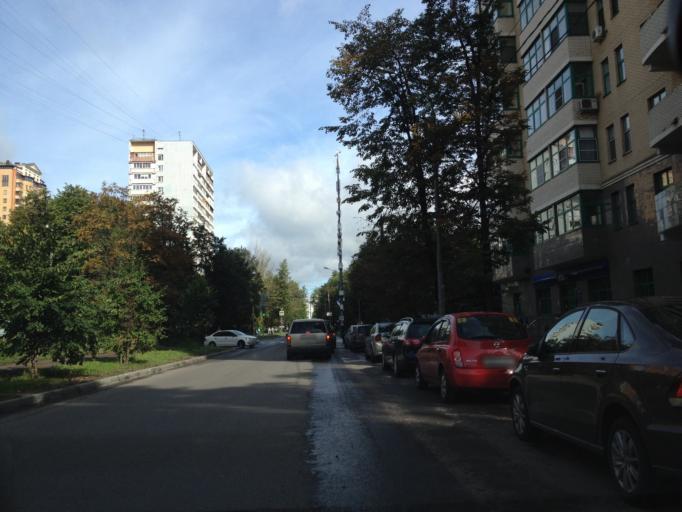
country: RU
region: Moskovskaya
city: Izmaylovo
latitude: 55.7960
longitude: 37.8055
